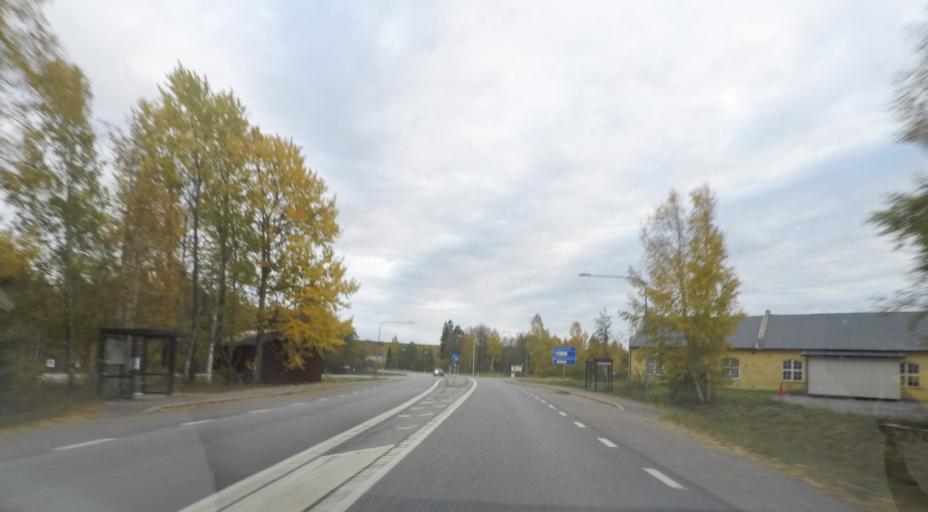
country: SE
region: OErebro
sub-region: Nora Kommun
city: As
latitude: 59.5096
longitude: 14.9649
